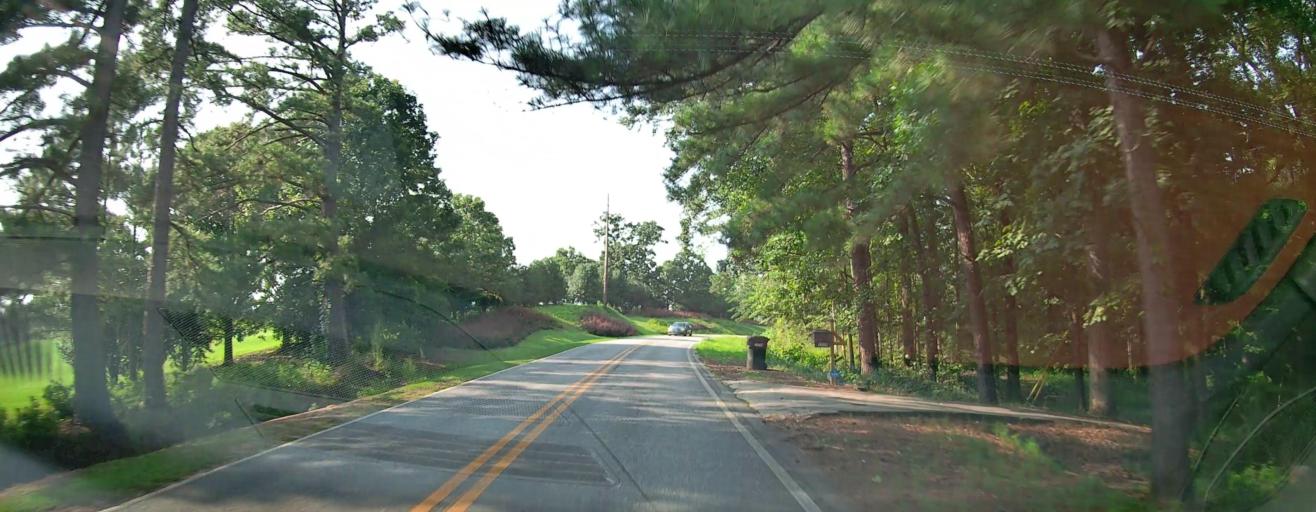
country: US
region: Georgia
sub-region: Bibb County
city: Macon
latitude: 32.9459
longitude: -83.7314
